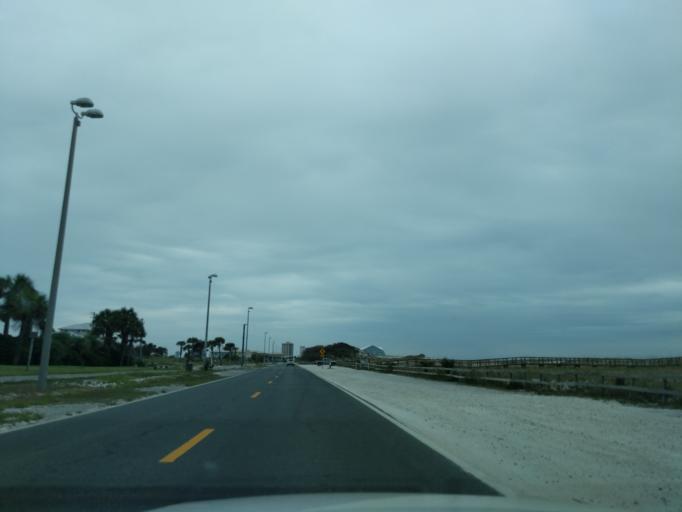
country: US
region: Florida
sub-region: Santa Rosa County
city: Gulf Breeze
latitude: 30.3283
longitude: -87.1616
